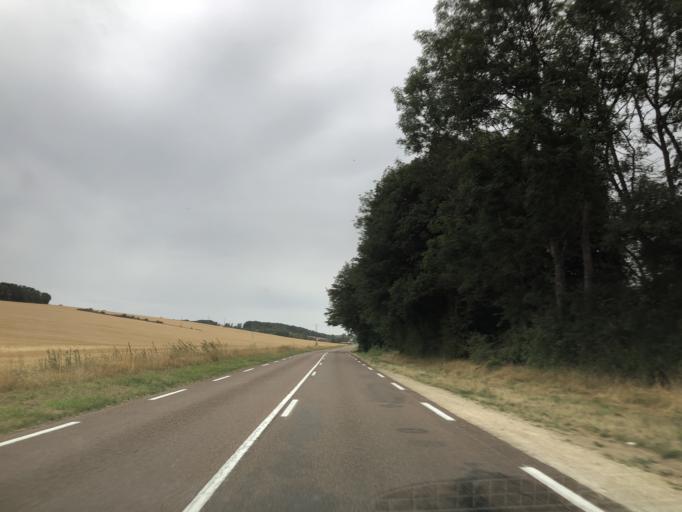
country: FR
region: Bourgogne
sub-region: Departement de l'Yonne
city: Saint-Julien-du-Sault
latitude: 47.9284
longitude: 3.2434
